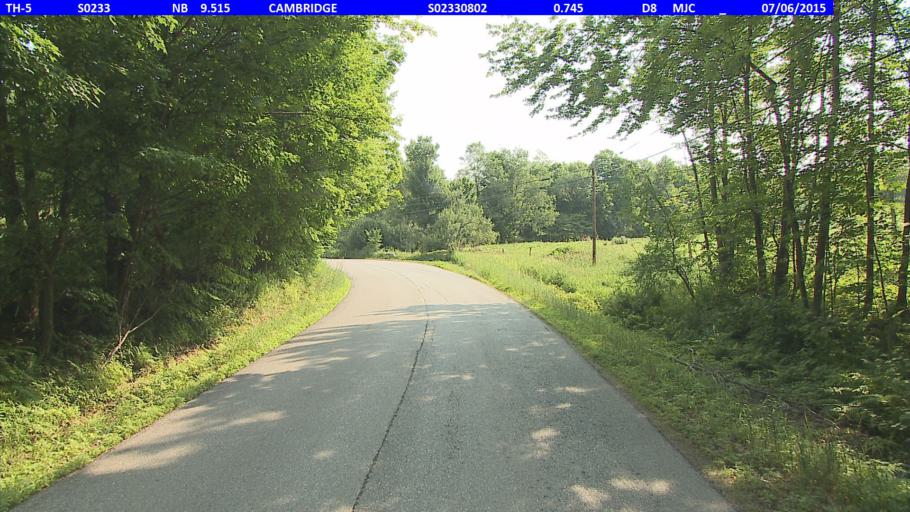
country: US
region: Vermont
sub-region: Chittenden County
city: Jericho
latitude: 44.5933
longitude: -72.8594
